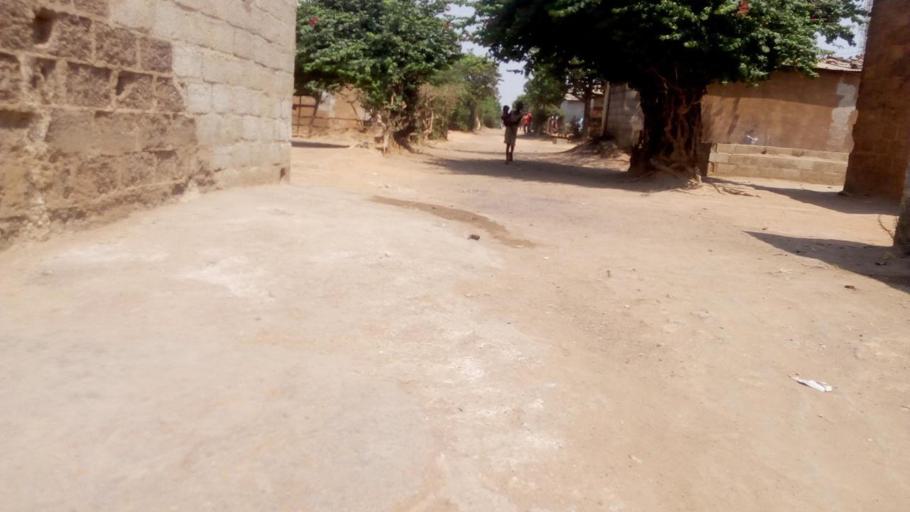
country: ZM
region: Lusaka
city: Lusaka
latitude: -15.3545
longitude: 28.2922
